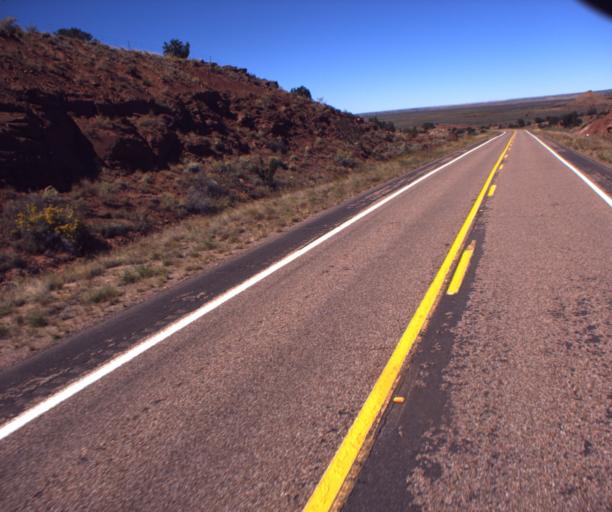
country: US
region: Arizona
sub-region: Apache County
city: Saint Johns
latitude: 34.5819
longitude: -109.5371
